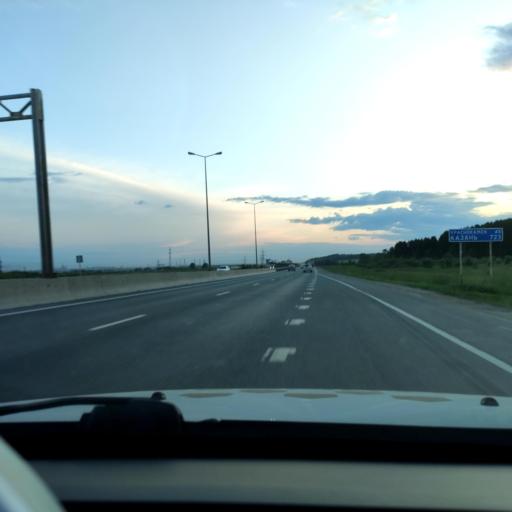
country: RU
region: Perm
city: Froly
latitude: 57.9339
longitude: 56.2592
